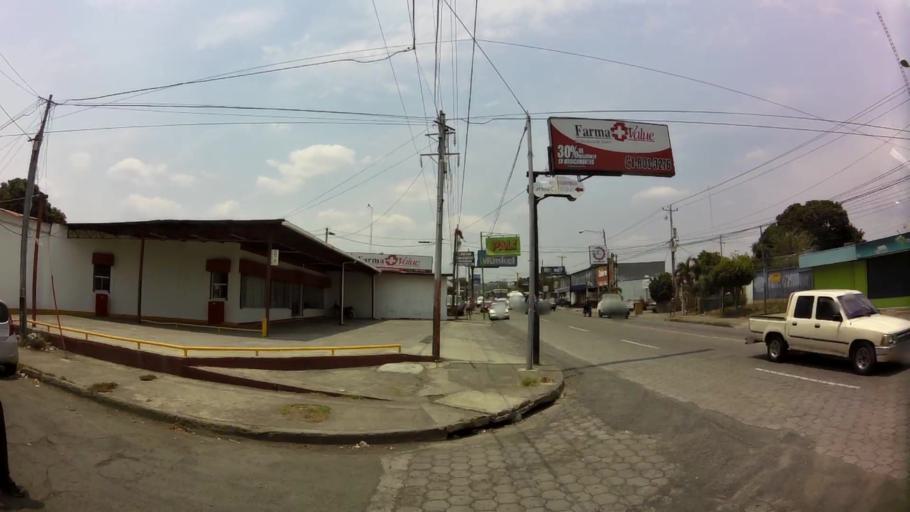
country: NI
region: Managua
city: Ciudad Sandino
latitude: 12.1482
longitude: -86.3047
